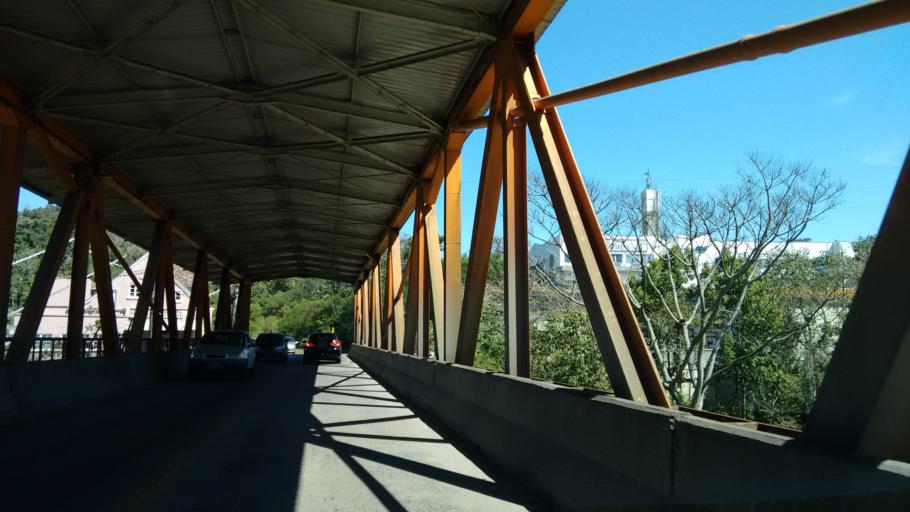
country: BR
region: Santa Catarina
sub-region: Blumenau
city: Blumenau
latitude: -26.8811
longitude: -49.1020
